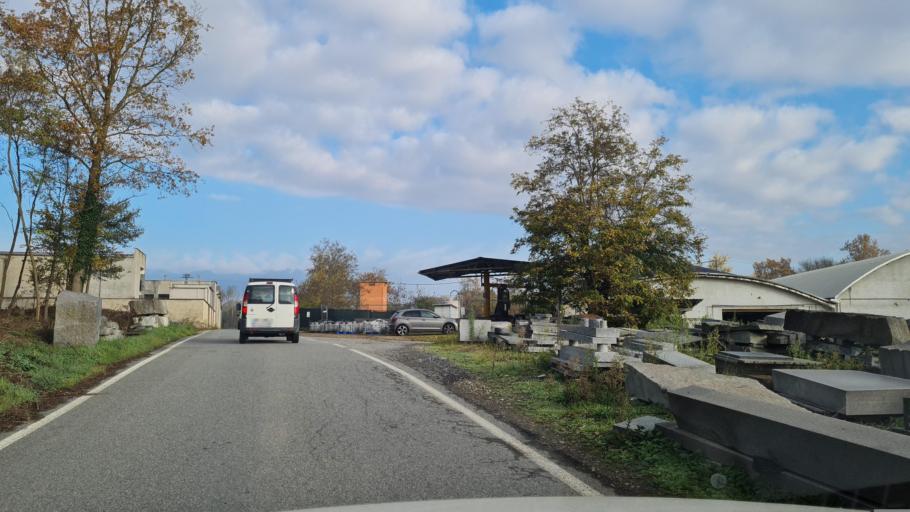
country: IT
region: Piedmont
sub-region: Provincia di Biella
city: Castelletto Cervo
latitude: 45.5149
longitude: 8.2303
